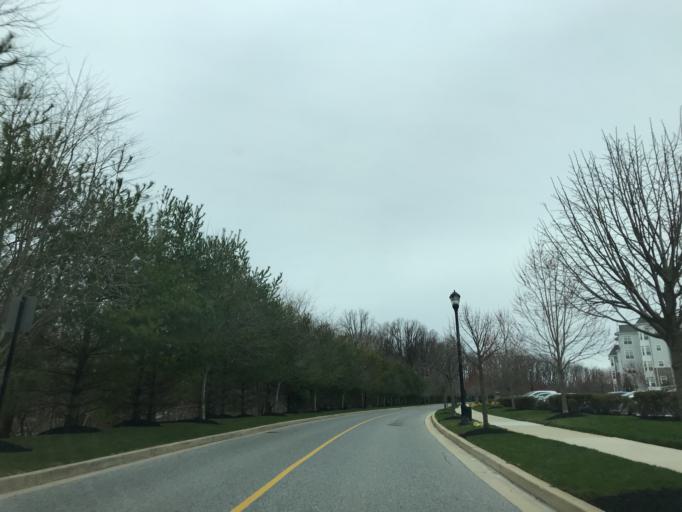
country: US
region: Maryland
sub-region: Baltimore County
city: Pikesville
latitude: 39.3804
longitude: -76.6930
